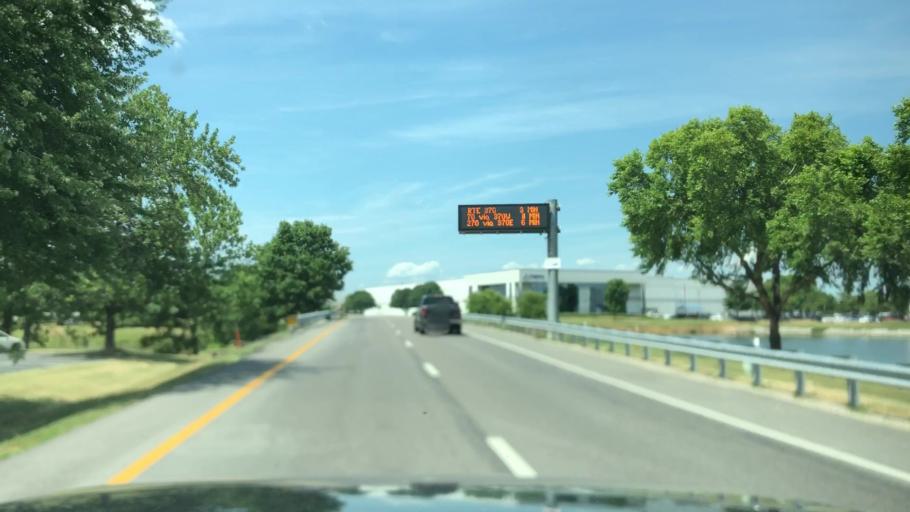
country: US
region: Missouri
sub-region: Saint Charles County
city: Saint Charles
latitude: 38.7683
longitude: -90.4567
